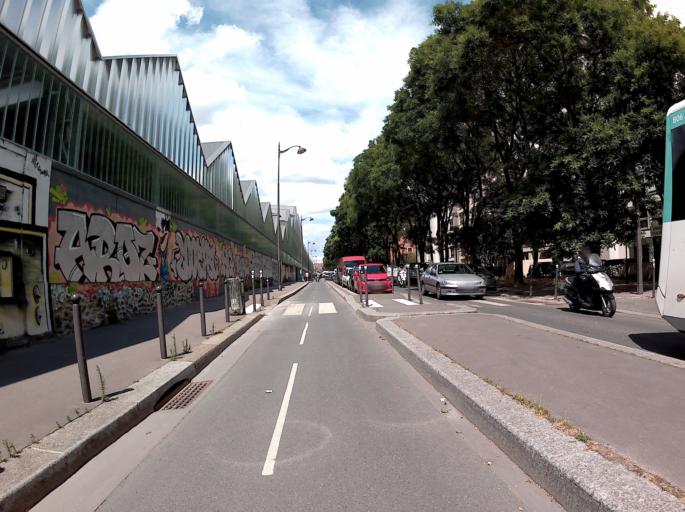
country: FR
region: Ile-de-France
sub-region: Departement de Seine-Saint-Denis
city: Aubervilliers
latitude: 48.8908
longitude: 2.3686
